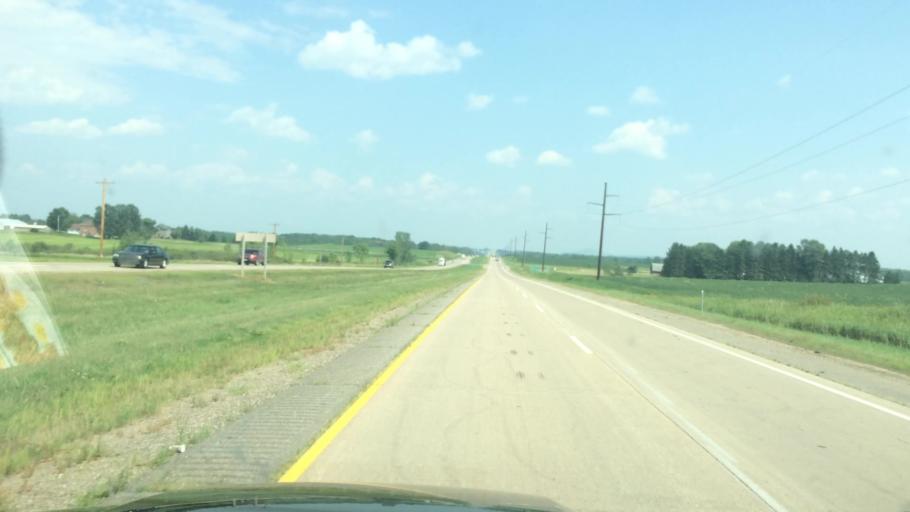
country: US
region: Wisconsin
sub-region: Marathon County
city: Edgar
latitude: 44.9442
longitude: -90.0015
